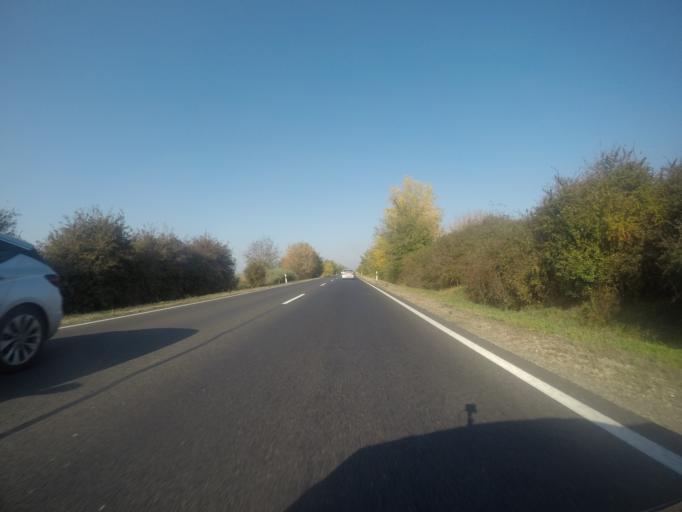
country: HU
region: Fejer
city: Baracs
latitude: 46.8881
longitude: 18.9198
